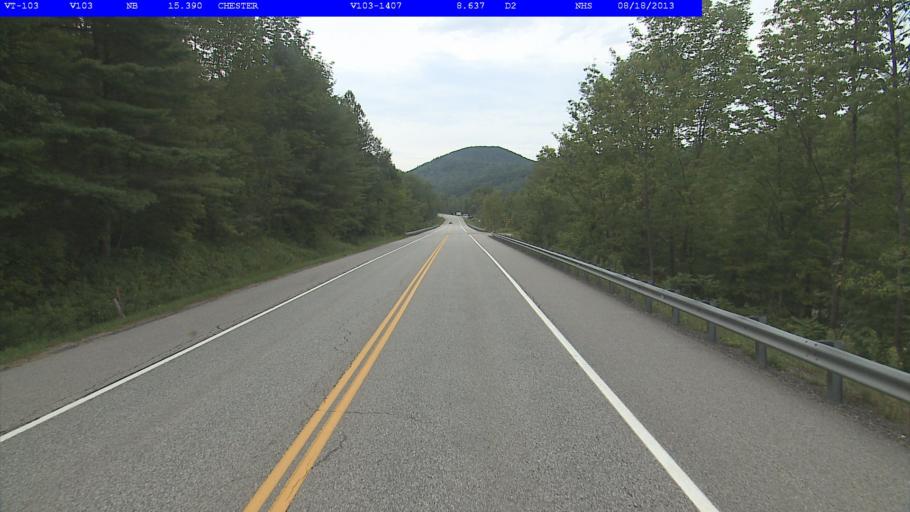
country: US
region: Vermont
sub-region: Windsor County
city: Chester
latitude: 43.3352
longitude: -72.6164
